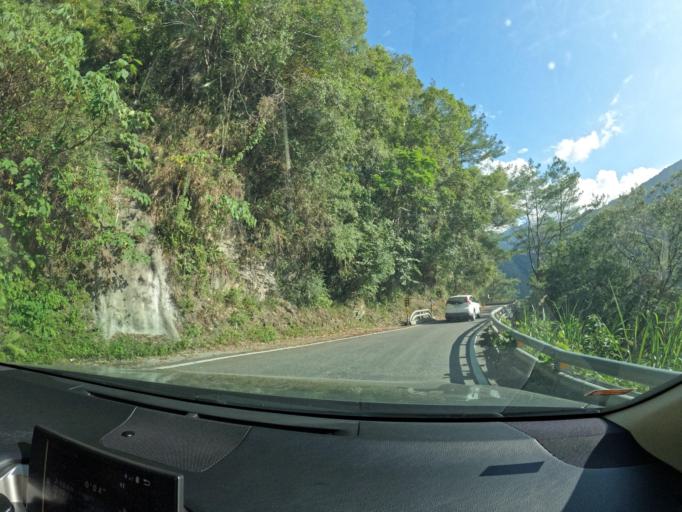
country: TW
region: Taiwan
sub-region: Taitung
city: Taitung
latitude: 23.1916
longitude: 121.0187
